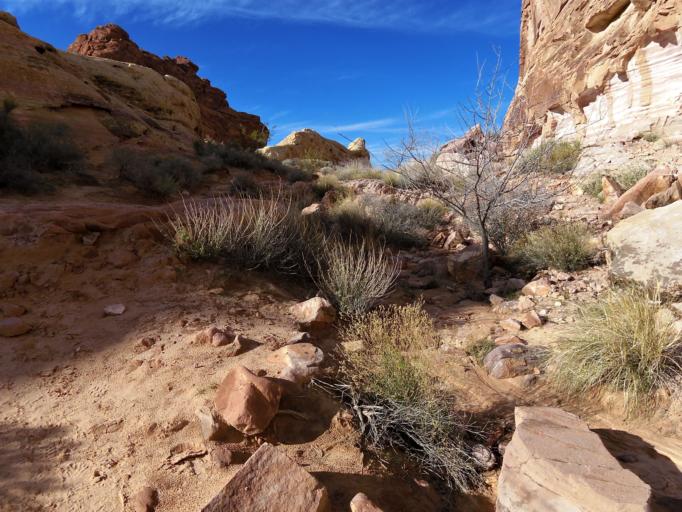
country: US
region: Nevada
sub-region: Clark County
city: Moapa Valley
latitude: 36.4831
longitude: -114.5348
